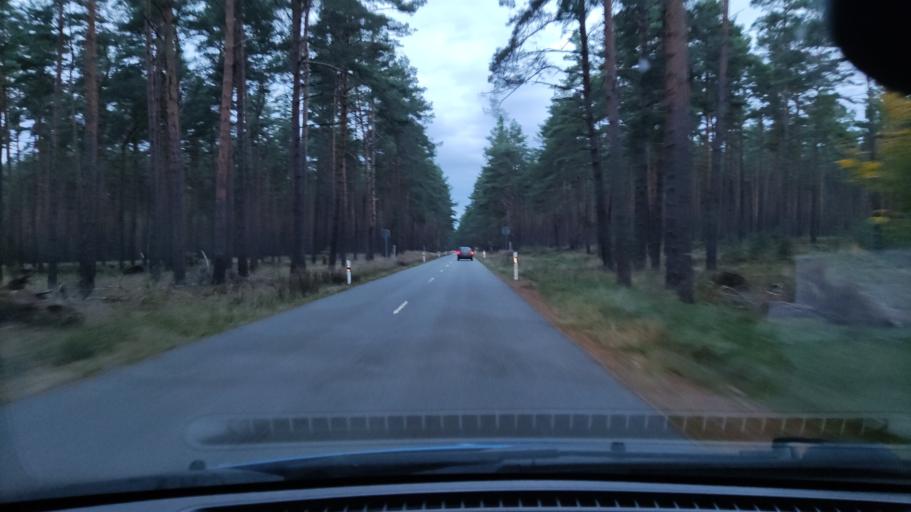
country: DE
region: Lower Saxony
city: Prezelle
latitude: 53.0126
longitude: 11.3891
